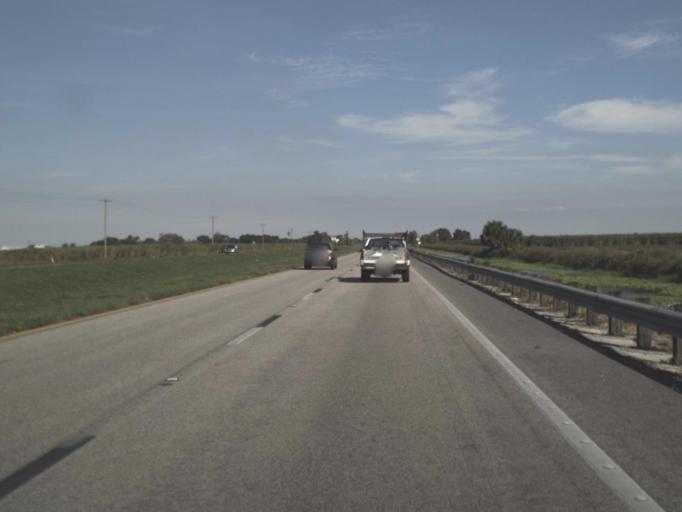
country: US
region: Florida
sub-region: Hendry County
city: Harlem
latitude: 26.7540
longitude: -81.0060
